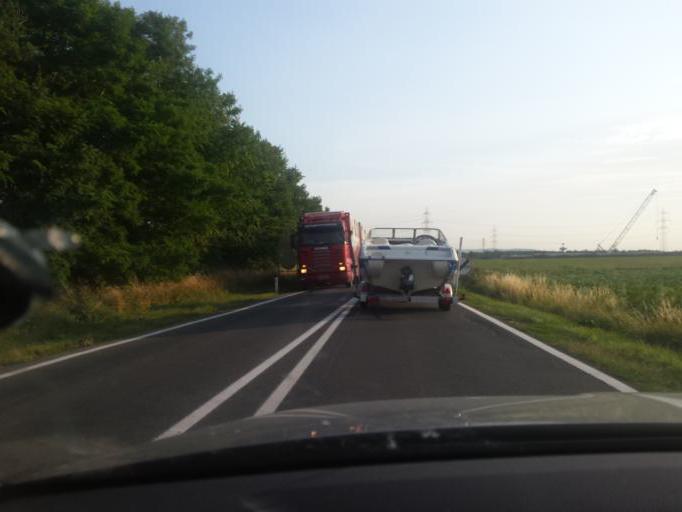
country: AT
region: Lower Austria
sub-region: Politischer Bezirk Bruck an der Leitha
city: Rohrau
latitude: 48.0407
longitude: 16.8239
